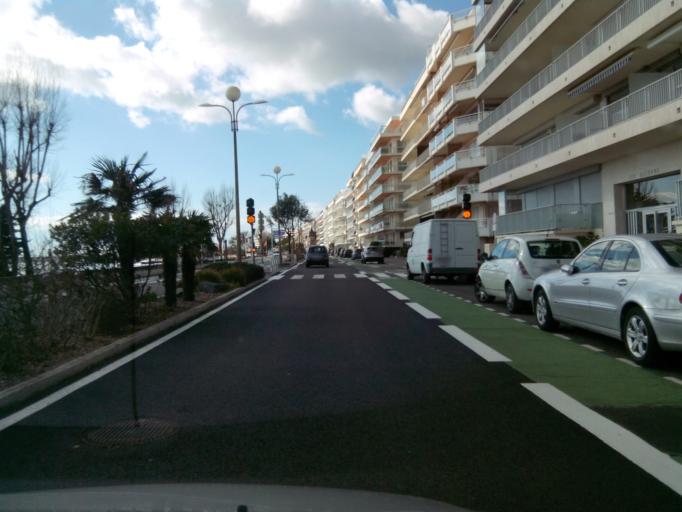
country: FR
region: Pays de la Loire
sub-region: Departement de la Loire-Atlantique
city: La Baule-Escoublac
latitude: 47.2819
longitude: -2.3956
